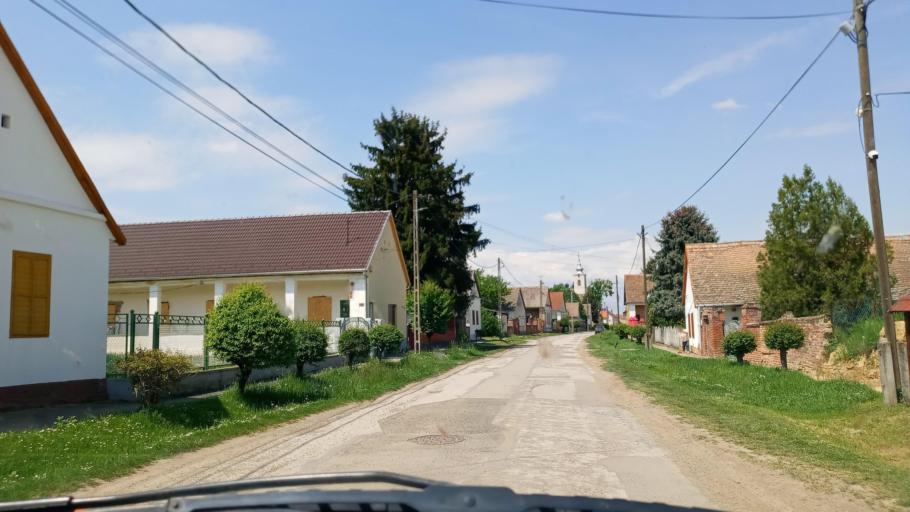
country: HU
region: Baranya
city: Villany
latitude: 45.8721
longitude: 18.5111
